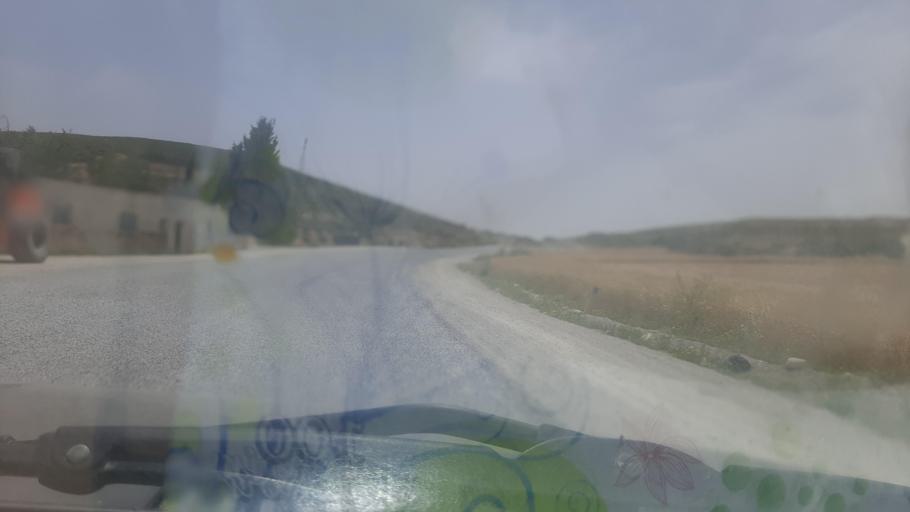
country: TN
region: Zaghwan
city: Zaghouan
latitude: 36.5365
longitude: 10.1544
